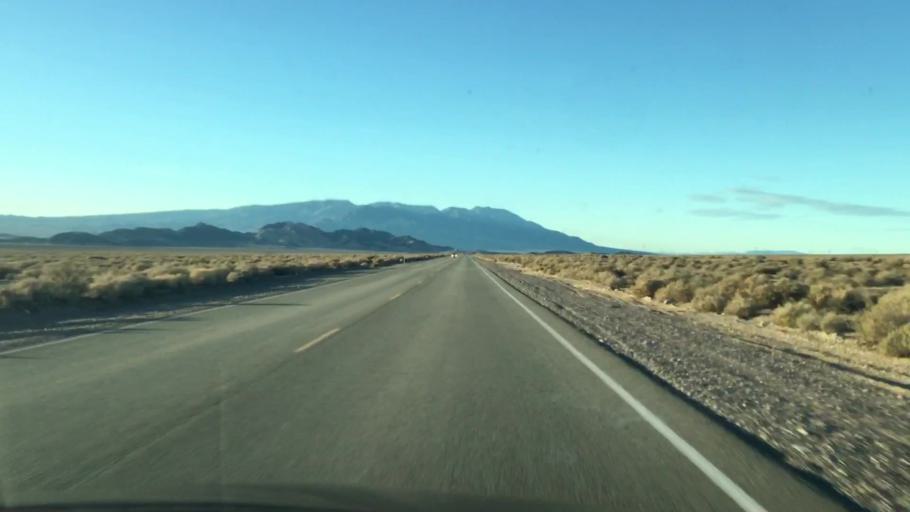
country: US
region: California
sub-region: San Bernardino County
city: Fort Irwin
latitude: 35.3523
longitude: -116.0925
